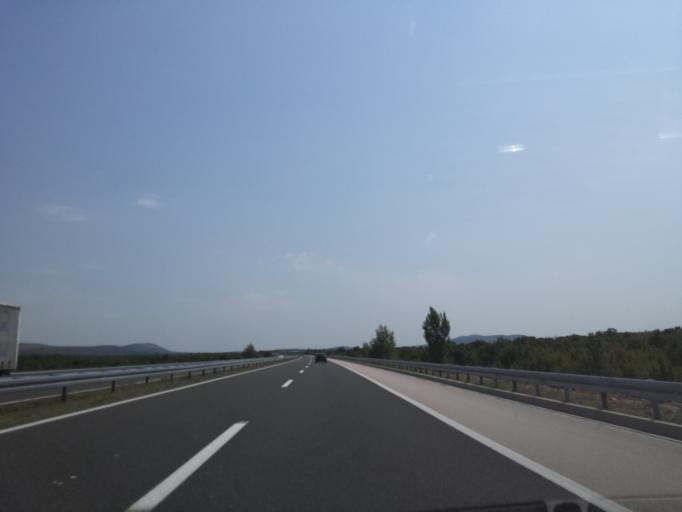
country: HR
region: Zadarska
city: Benkovac
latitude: 43.9677
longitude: 15.6524
